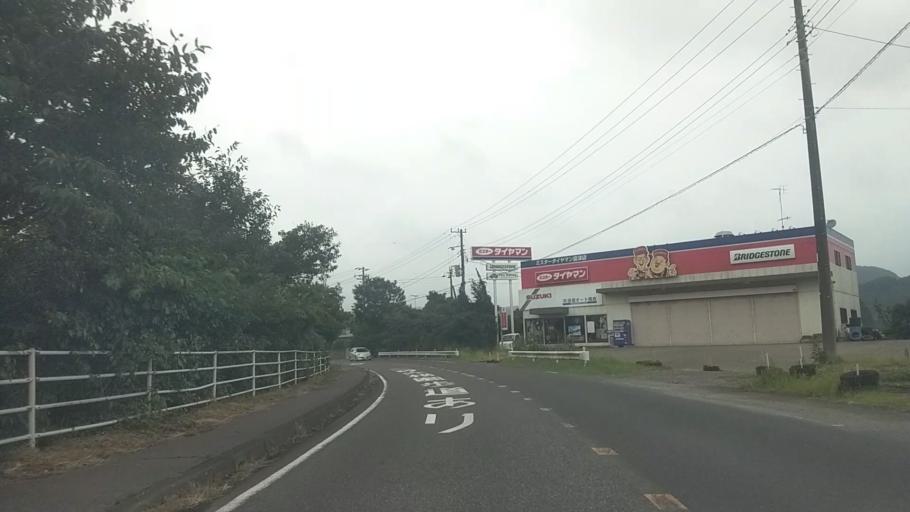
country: JP
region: Chiba
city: Kimitsu
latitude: 35.2173
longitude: 139.8916
